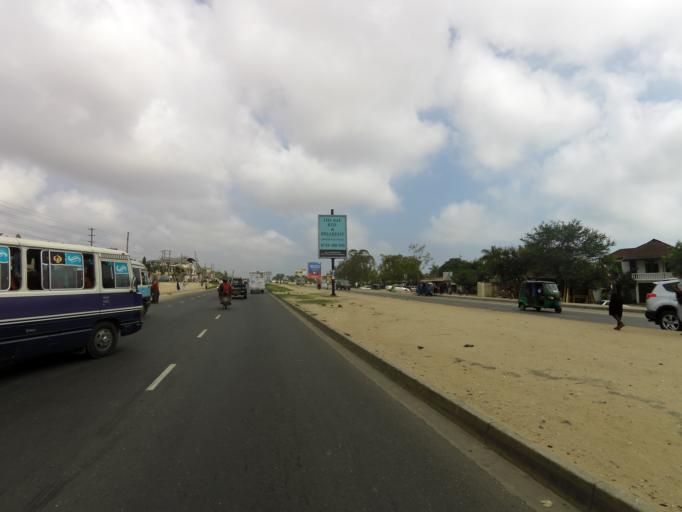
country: TZ
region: Dar es Salaam
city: Magomeni
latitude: -6.7176
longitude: 39.2114
